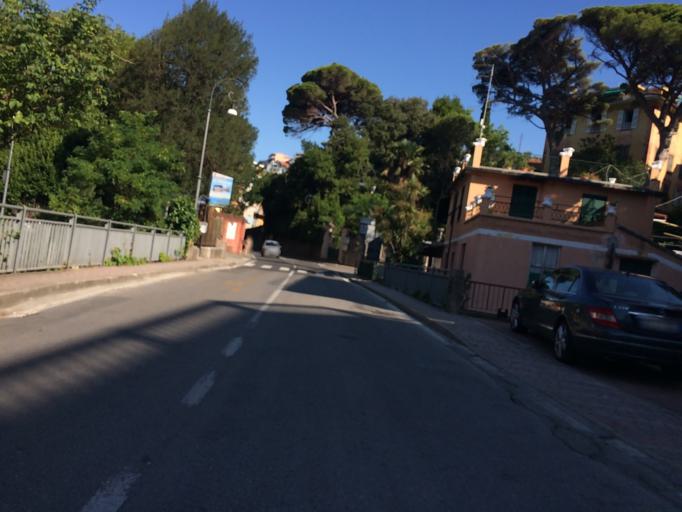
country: IT
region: Liguria
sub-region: Provincia di Genova
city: Rapallo
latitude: 44.3470
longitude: 9.2415
